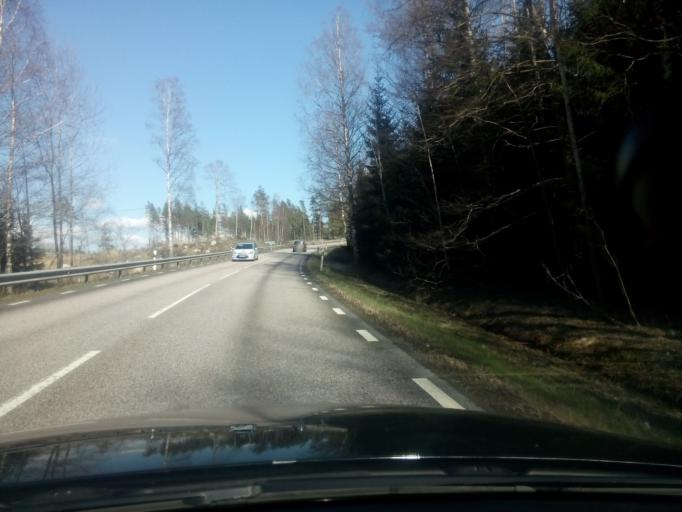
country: SE
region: Soedermanland
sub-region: Flens Kommun
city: Malmkoping
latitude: 59.2060
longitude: 16.7981
